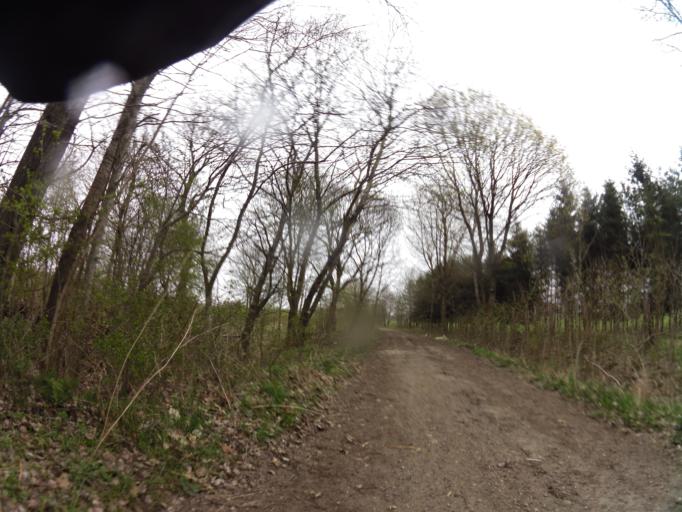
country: PL
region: West Pomeranian Voivodeship
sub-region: Powiat koszalinski
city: Bobolice
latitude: 53.9874
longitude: 16.6767
